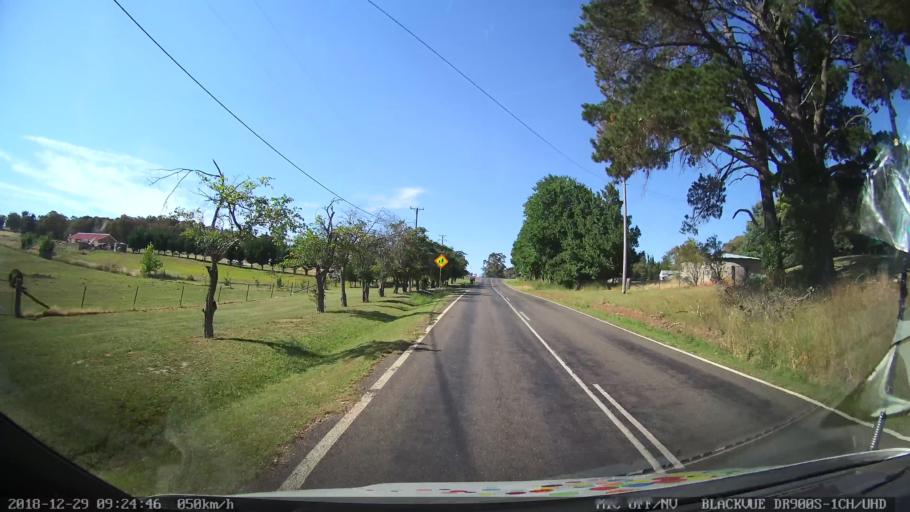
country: AU
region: New South Wales
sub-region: Upper Lachlan Shire
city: Crookwell
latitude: -34.5392
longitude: 149.3937
